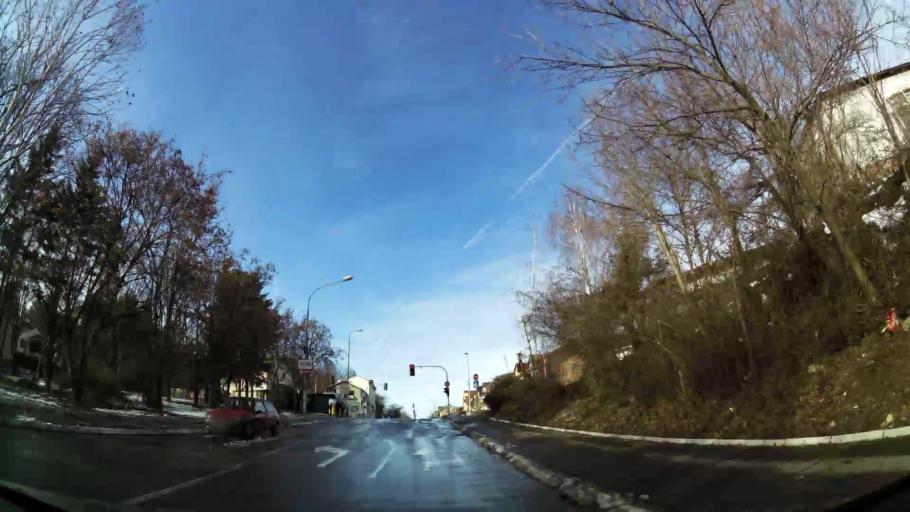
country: RS
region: Central Serbia
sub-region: Belgrade
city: Rakovica
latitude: 44.7256
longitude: 20.4270
